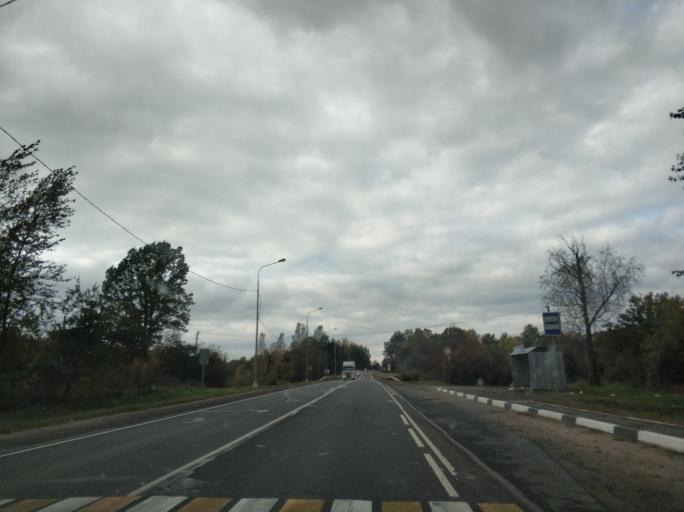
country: RU
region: Pskov
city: Ostrov
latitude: 57.3013
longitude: 28.3731
